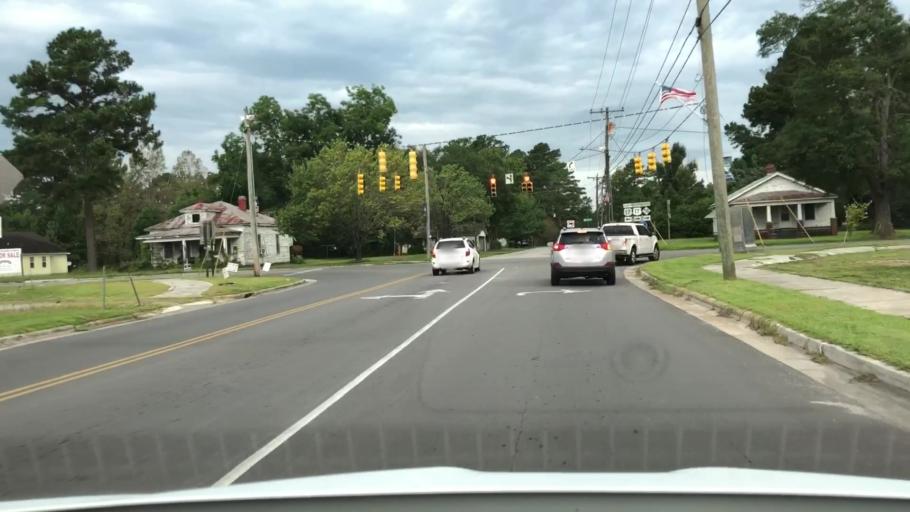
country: US
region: North Carolina
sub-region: Jones County
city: Maysville
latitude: 34.9016
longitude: -77.2310
